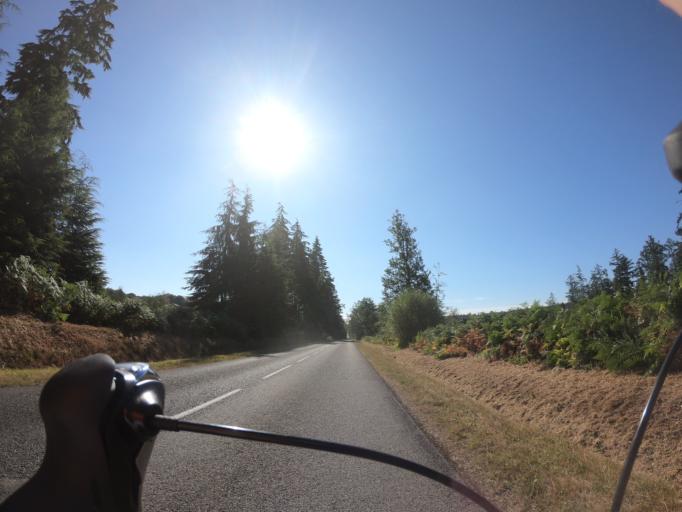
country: FR
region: Lower Normandy
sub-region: Departement de l'Orne
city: Juvigny-sous-Andaine
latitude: 48.5865
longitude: -0.4868
